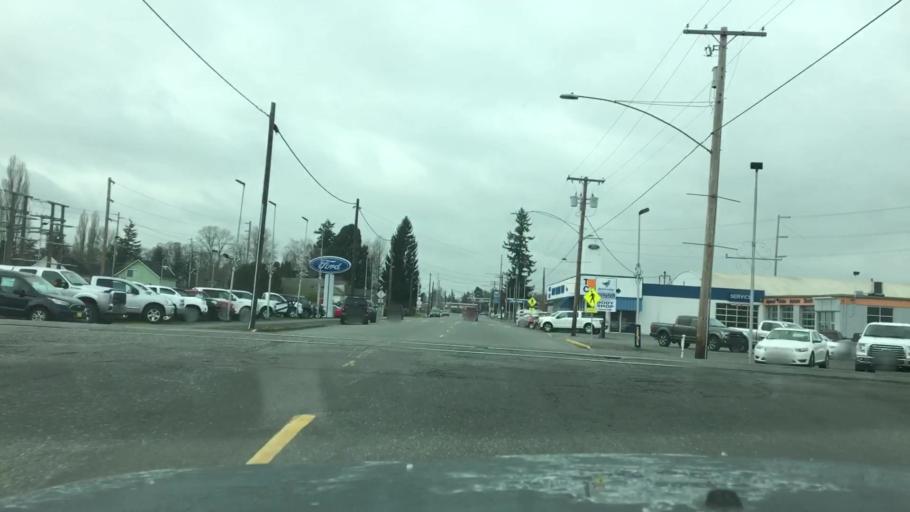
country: US
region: Washington
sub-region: Skagit County
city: Sedro-Woolley
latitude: 48.5054
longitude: -122.2404
